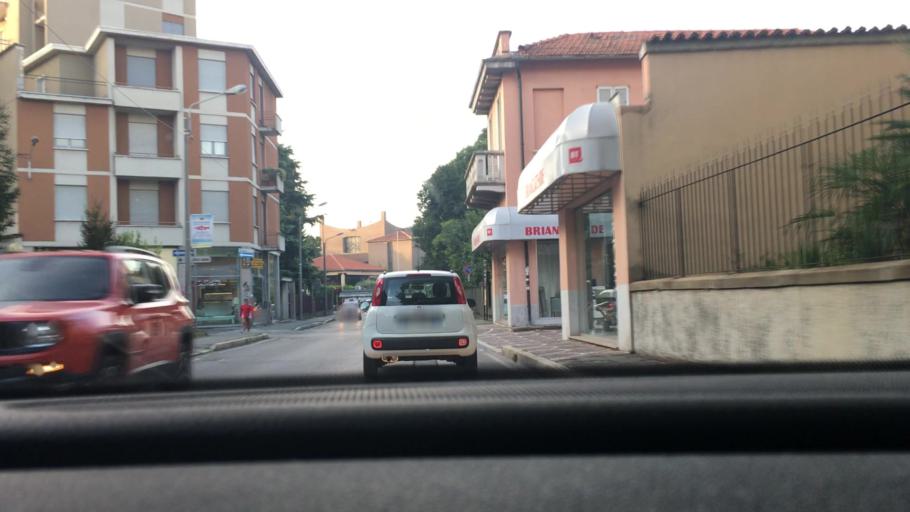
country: IT
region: Lombardy
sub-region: Provincia di Monza e Brianza
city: Monza
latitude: 45.5890
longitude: 9.2661
